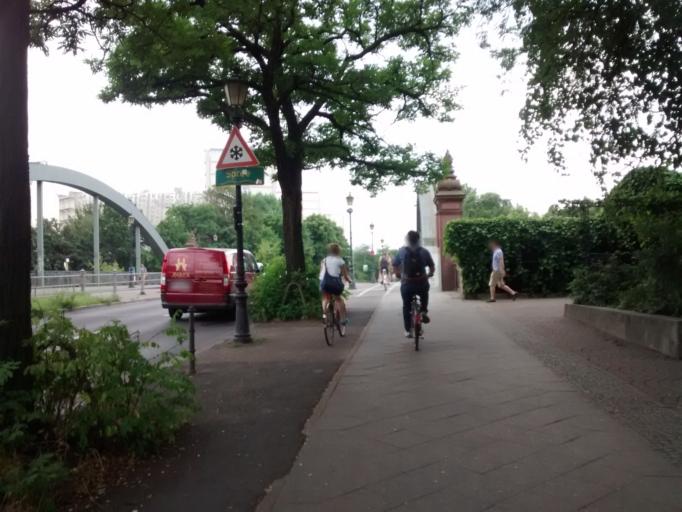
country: DE
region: Berlin
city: Moabit
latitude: 52.5290
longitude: 13.3435
